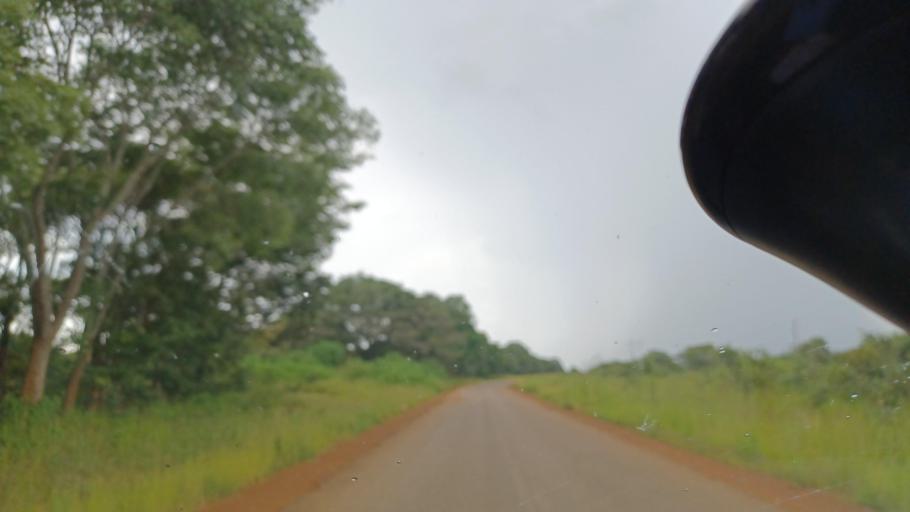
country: ZM
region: North-Western
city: Kasempa
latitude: -13.0454
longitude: 25.9917
